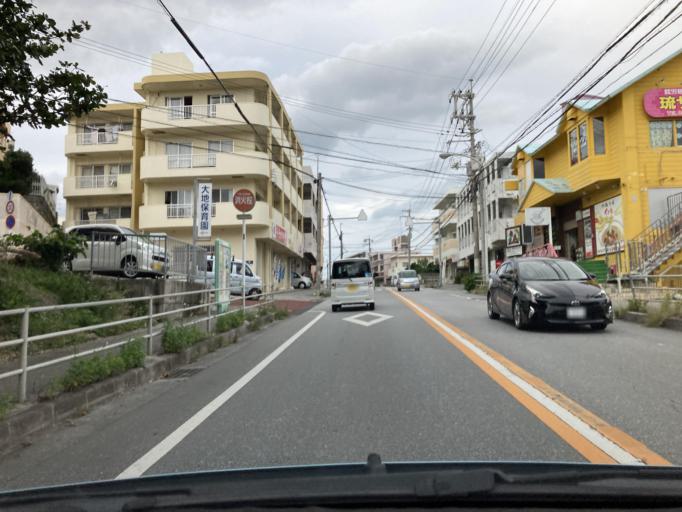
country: JP
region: Okinawa
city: Tomigusuku
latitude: 26.1837
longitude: 127.6822
